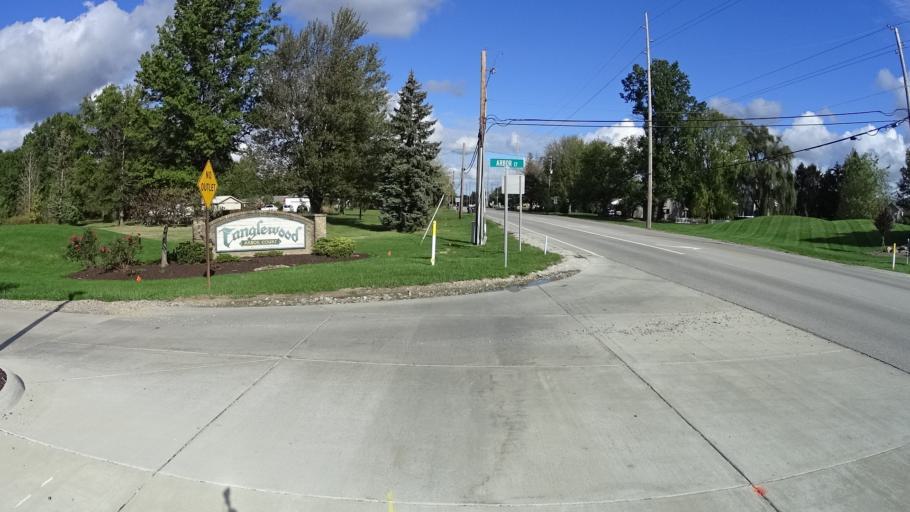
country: US
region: Ohio
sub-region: Lorain County
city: Grafton
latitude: 41.2918
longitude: -82.0669
